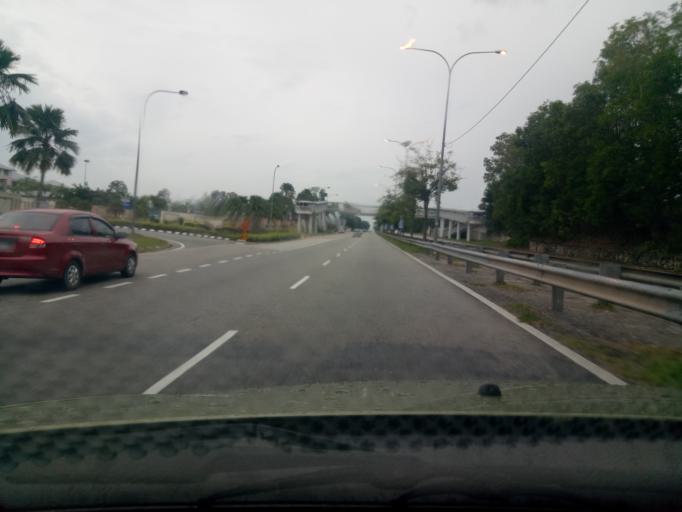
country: MY
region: Kedah
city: Sungai Petani
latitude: 5.6682
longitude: 100.5158
